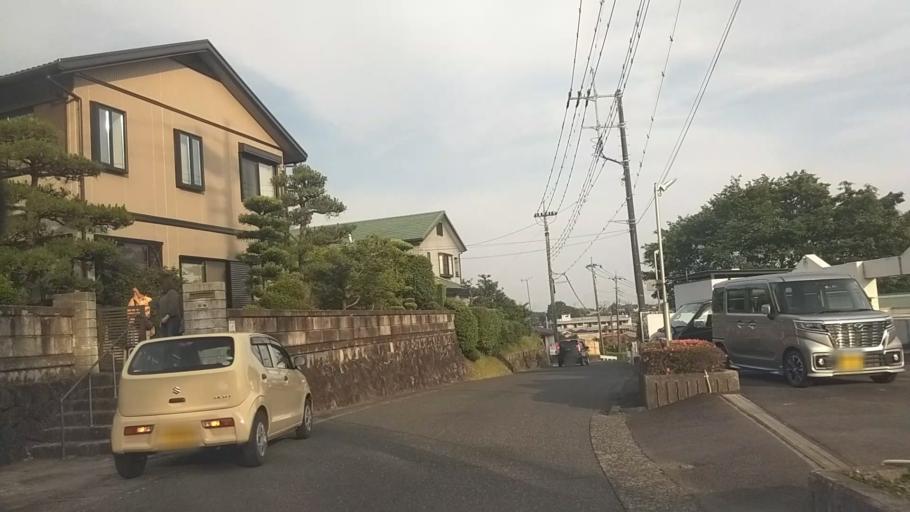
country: JP
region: Kanagawa
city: Odawara
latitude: 35.3169
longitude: 139.1154
